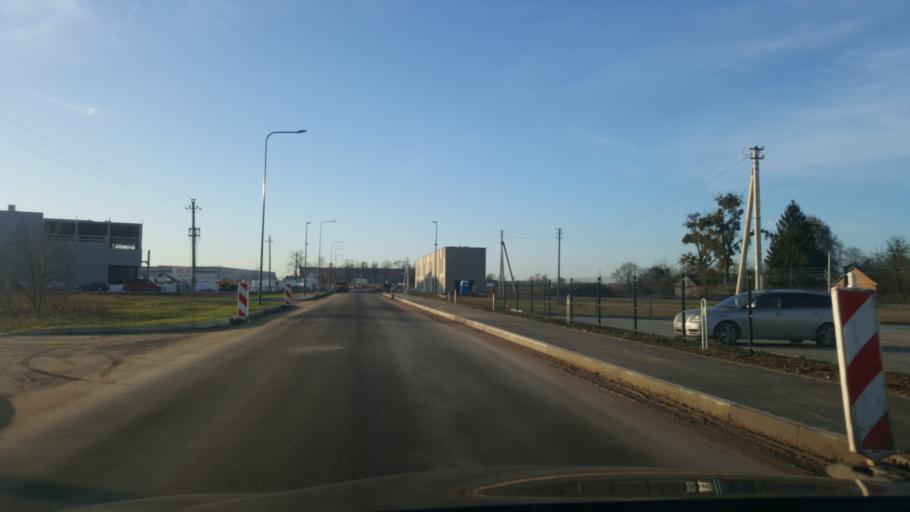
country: LT
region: Kauno apskritis
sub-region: Kauno rajonas
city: Mastaiciai
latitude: 54.8530
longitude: 23.8469
